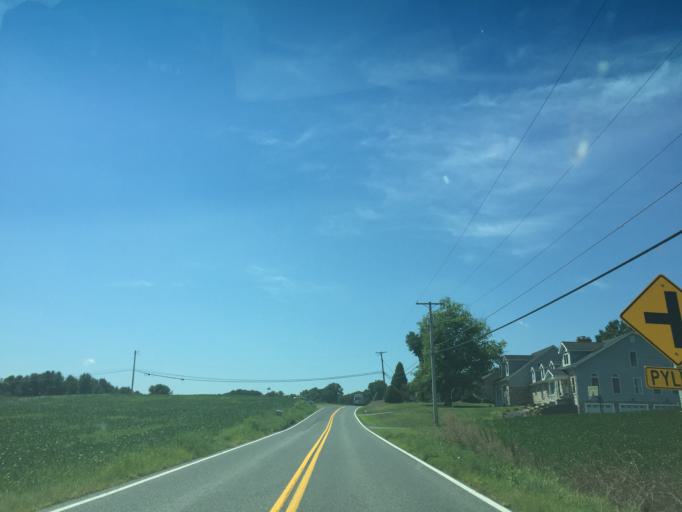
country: US
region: Maryland
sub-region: Harford County
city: Bel Air North
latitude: 39.6149
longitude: -76.3768
